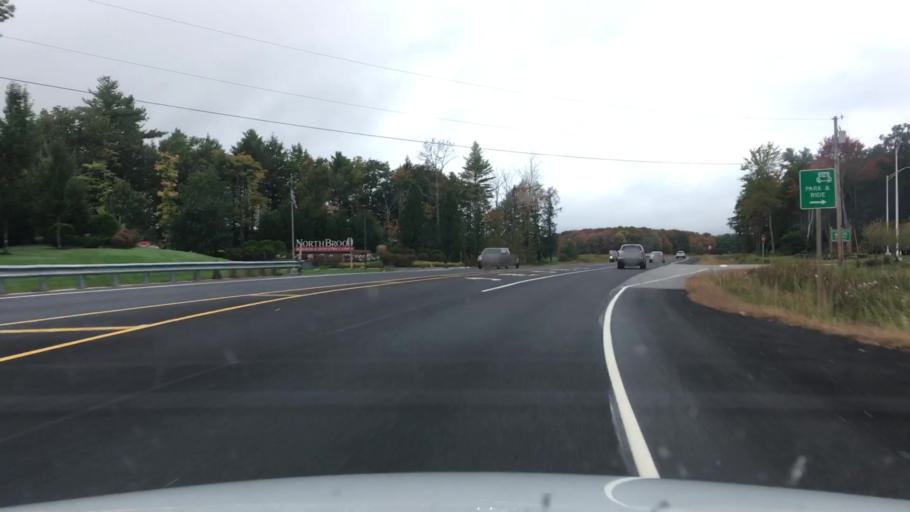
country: US
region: Maine
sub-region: Cumberland County
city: New Gloucester
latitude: 43.8858
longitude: -70.3406
